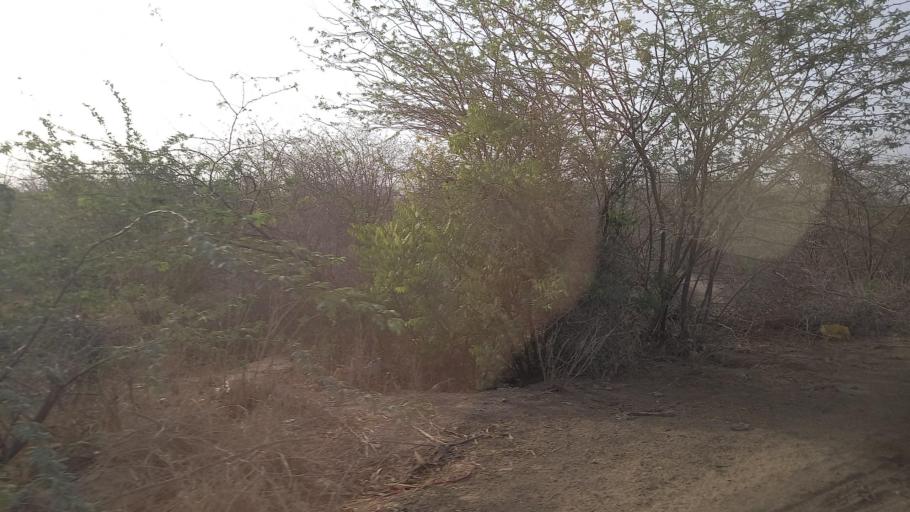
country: PK
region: Sindh
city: Malir Cantonment
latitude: 25.1145
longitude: 67.1915
